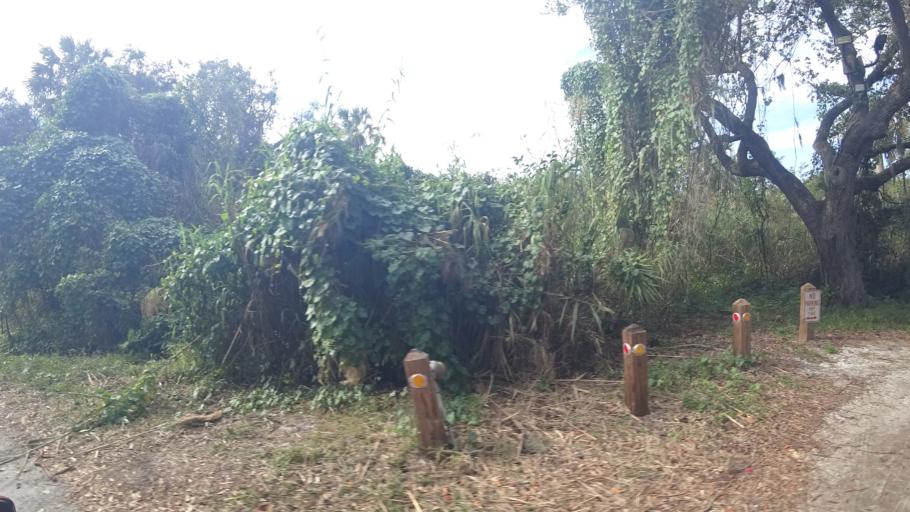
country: US
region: Florida
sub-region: Manatee County
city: West Bradenton
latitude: 27.5216
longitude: -82.6446
